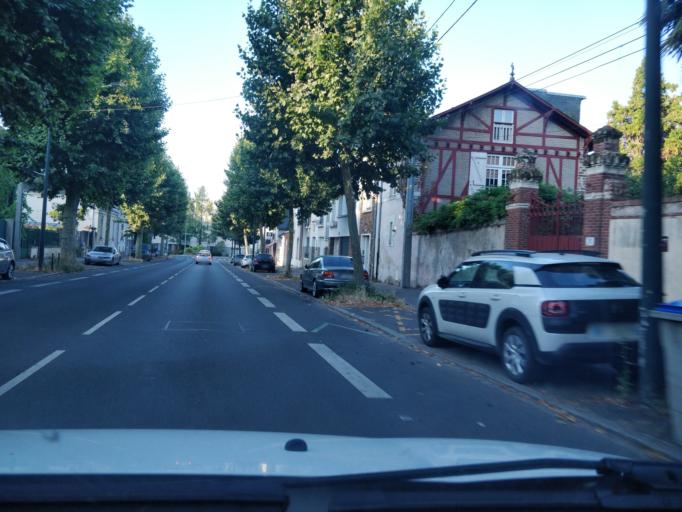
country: FR
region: Pays de la Loire
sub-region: Departement de la Loire-Atlantique
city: Nantes
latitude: 47.2354
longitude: -1.5634
